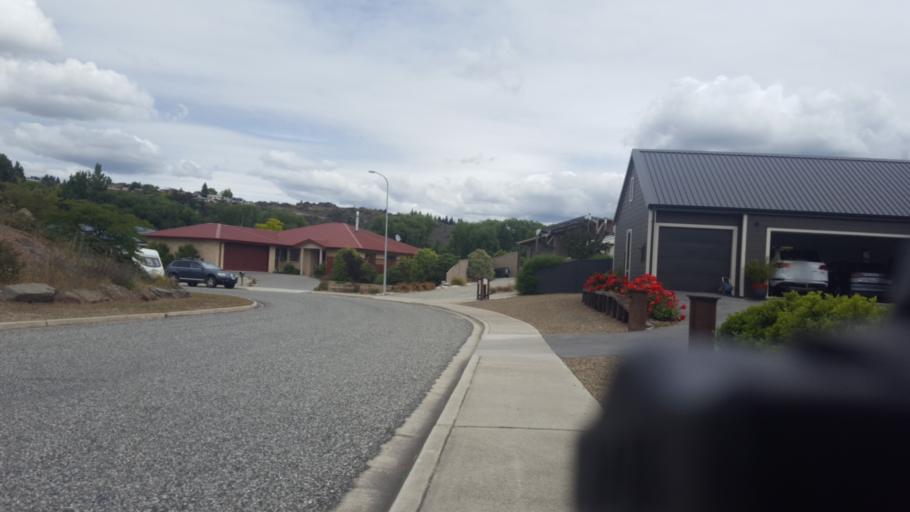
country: NZ
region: Otago
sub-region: Queenstown-Lakes District
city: Wanaka
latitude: -45.2527
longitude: 169.3816
